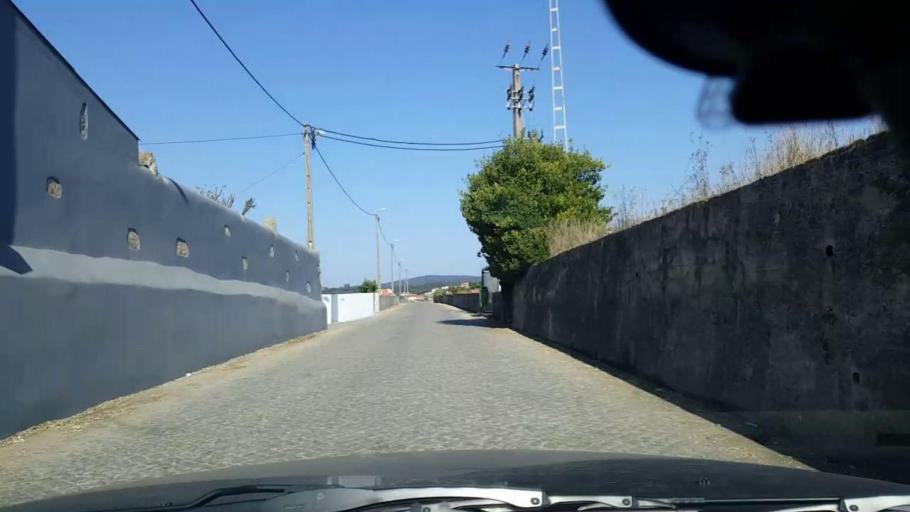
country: PT
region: Porto
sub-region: Vila do Conde
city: Arvore
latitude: 41.3583
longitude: -8.7102
